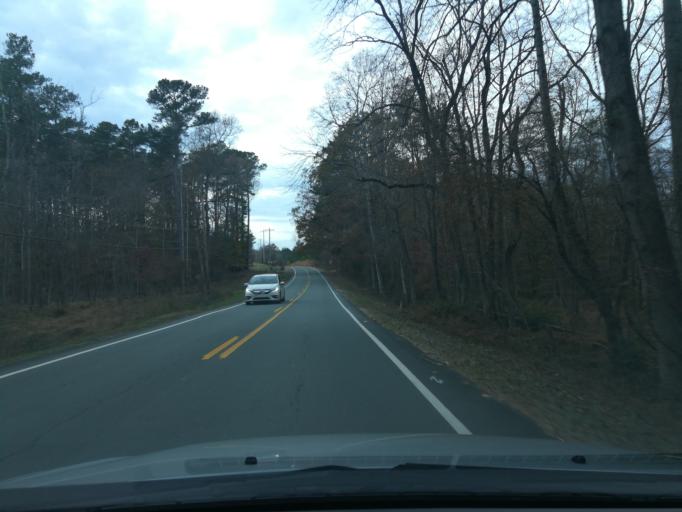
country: US
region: North Carolina
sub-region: Orange County
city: Hillsborough
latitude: 36.0306
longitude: -79.0176
